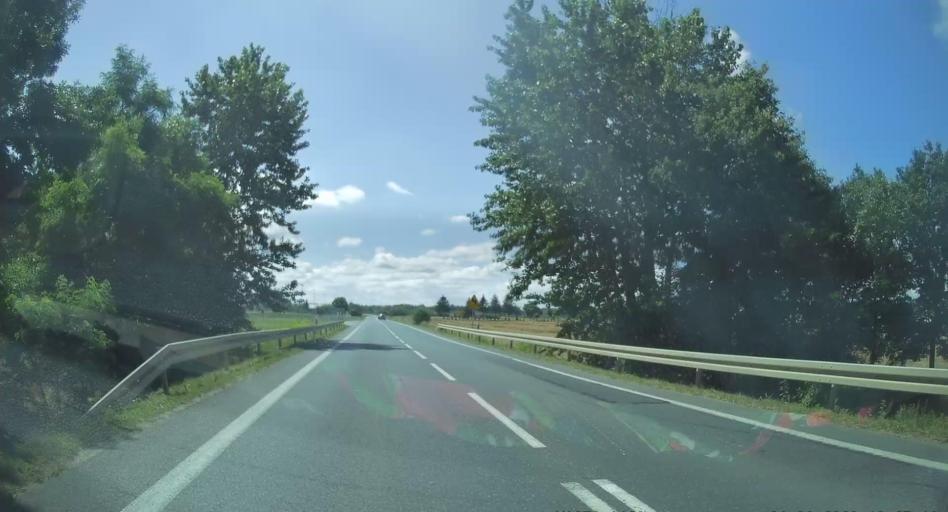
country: PL
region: Subcarpathian Voivodeship
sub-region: Powiat debicki
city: Brzeznica
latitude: 50.1450
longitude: 21.4860
